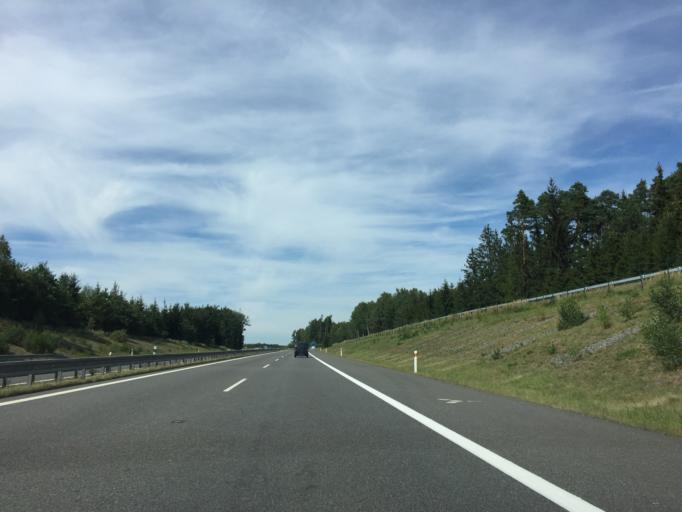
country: CZ
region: Jihocesky
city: Plana nad Luznici
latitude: 49.3582
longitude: 14.7247
